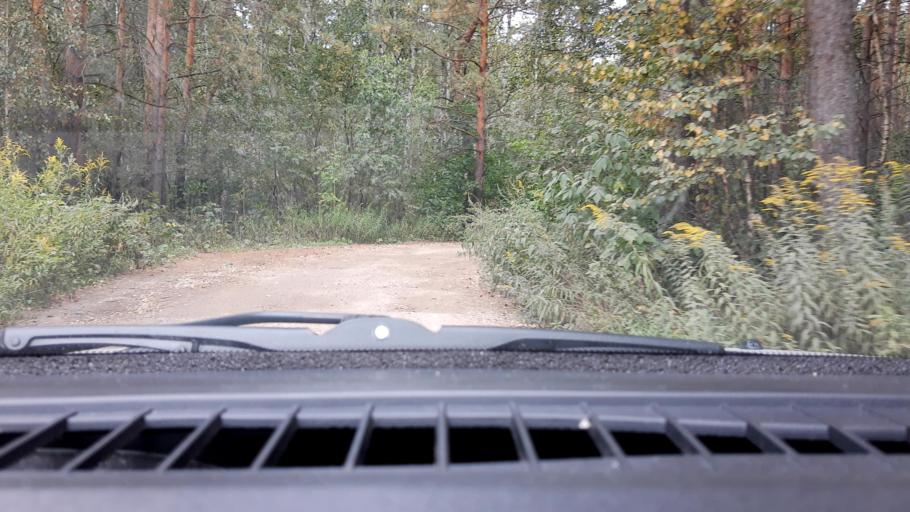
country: RU
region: Nizjnij Novgorod
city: Gorbatovka
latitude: 56.3121
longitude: 43.6896
